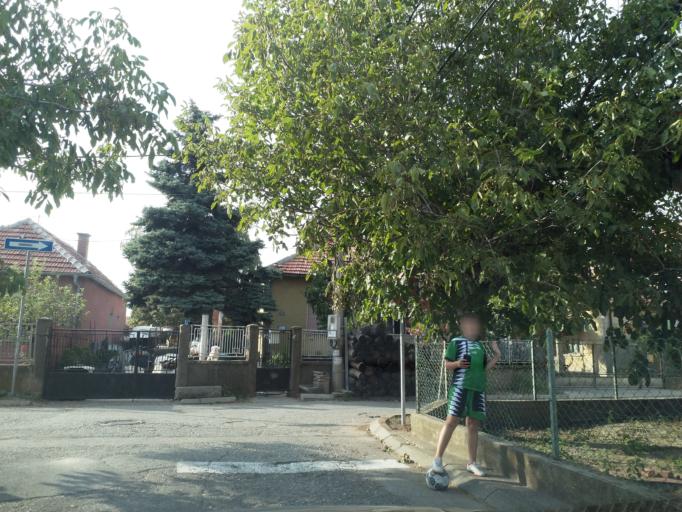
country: RS
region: Central Serbia
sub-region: Pomoravski Okrug
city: Paracin
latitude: 43.8661
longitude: 21.4114
